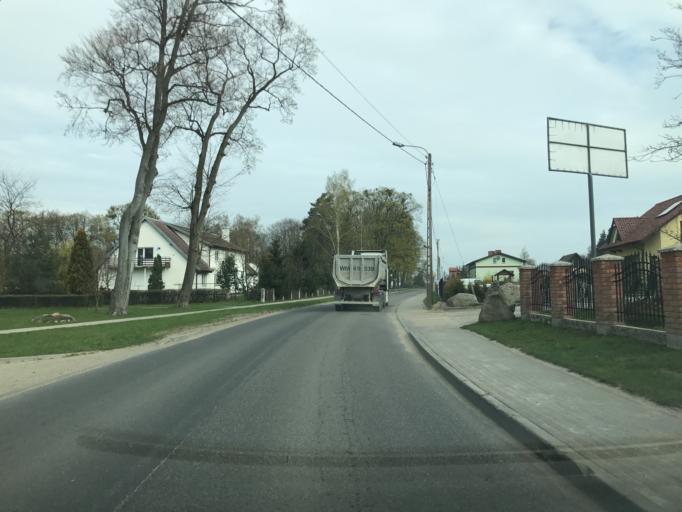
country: PL
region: Warmian-Masurian Voivodeship
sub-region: Powiat ostrodzki
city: Gierzwald
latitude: 53.5431
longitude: 20.0886
